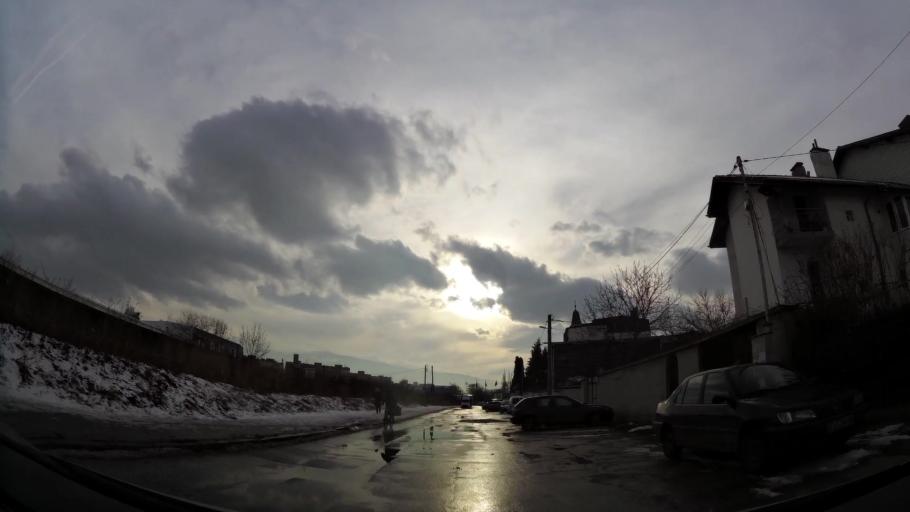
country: BG
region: Sofia-Capital
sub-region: Stolichna Obshtina
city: Sofia
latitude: 42.7123
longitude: 23.3476
